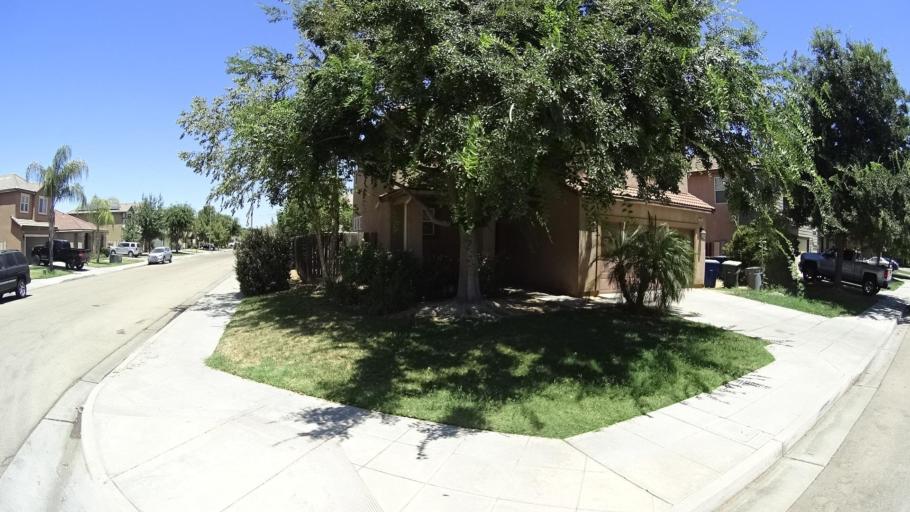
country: US
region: California
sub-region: Fresno County
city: Sunnyside
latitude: 36.7265
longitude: -119.6660
